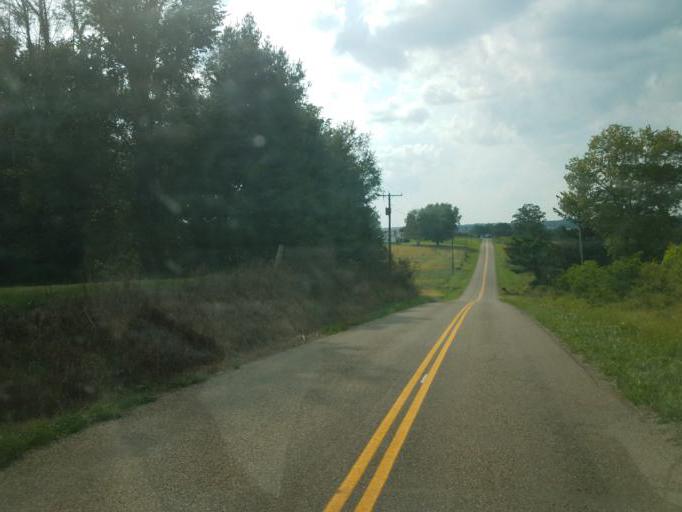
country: US
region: Ohio
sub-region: Knox County
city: Gambier
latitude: 40.3367
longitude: -82.3671
